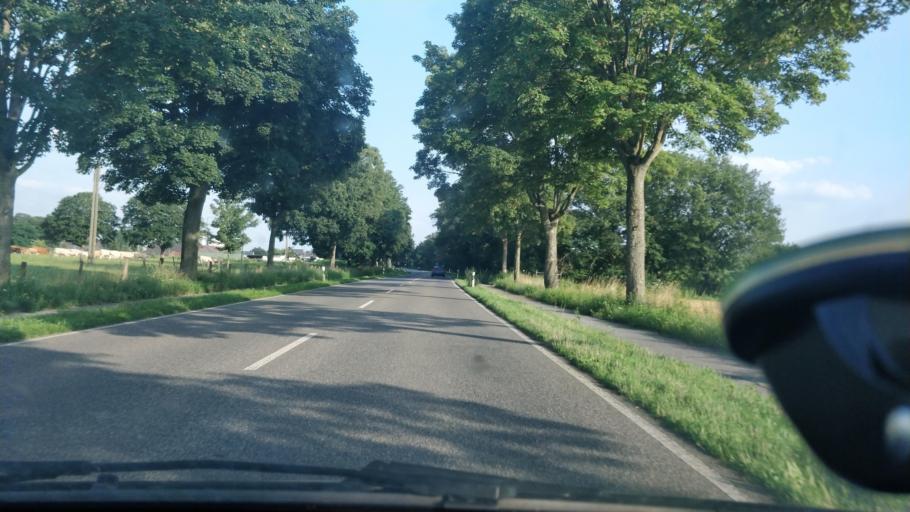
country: DE
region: North Rhine-Westphalia
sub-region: Regierungsbezirk Dusseldorf
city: Kamp-Lintfort
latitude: 51.5186
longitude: 6.5340
